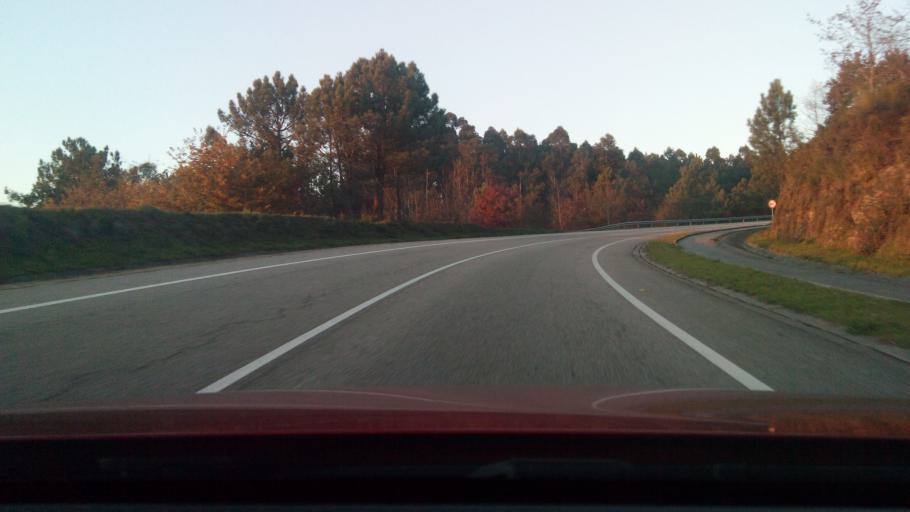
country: ES
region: Galicia
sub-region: Provincia de Pontevedra
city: Vigo
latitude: 42.1705
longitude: -8.6907
